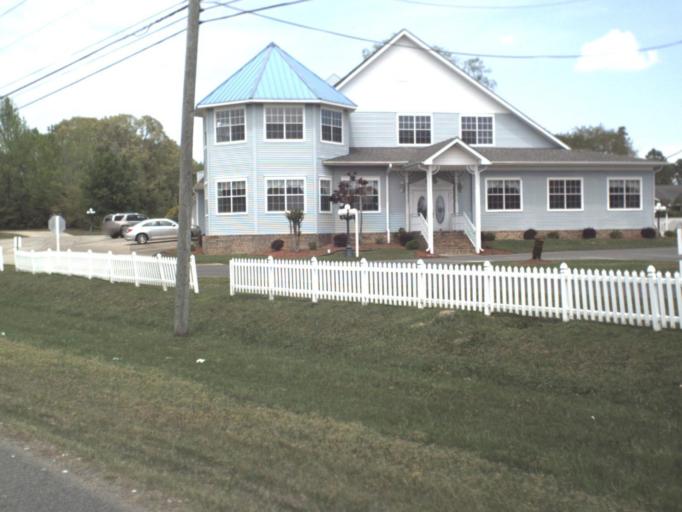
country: US
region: Florida
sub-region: Escambia County
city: Ensley
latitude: 30.5136
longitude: -87.3102
